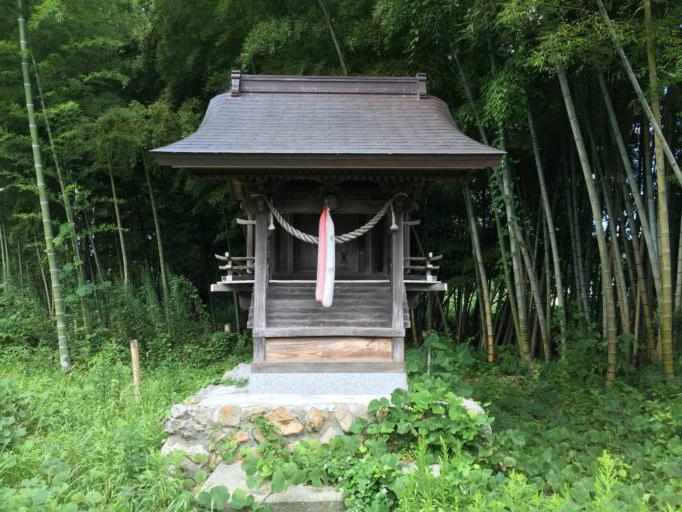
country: JP
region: Fukushima
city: Namie
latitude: 37.2859
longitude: 141.0012
